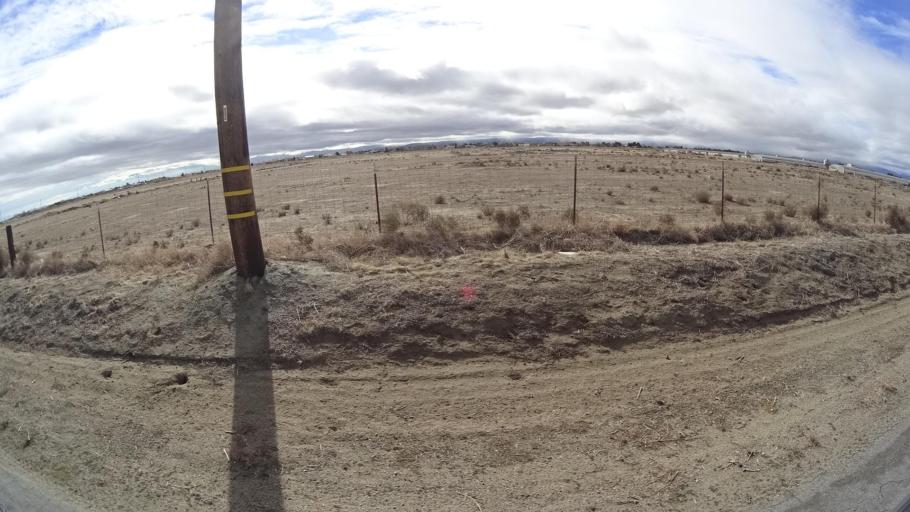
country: US
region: California
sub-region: Kern County
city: Rosamond
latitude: 34.8346
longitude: -118.2610
